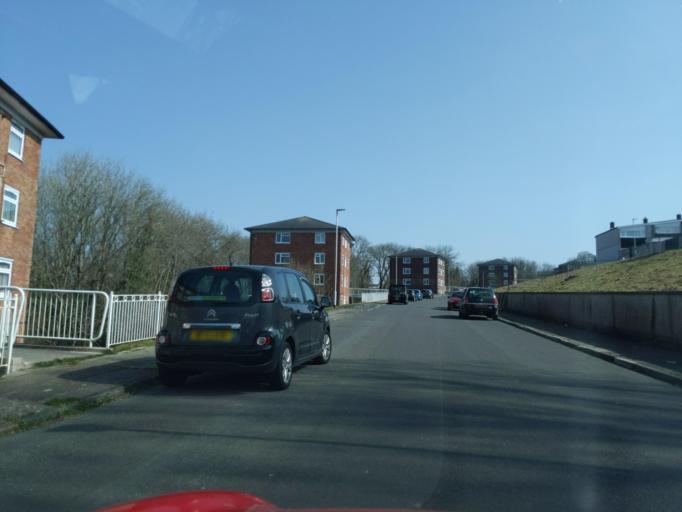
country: GB
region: England
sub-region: Plymouth
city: Plymouth
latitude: 50.4315
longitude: -4.1327
